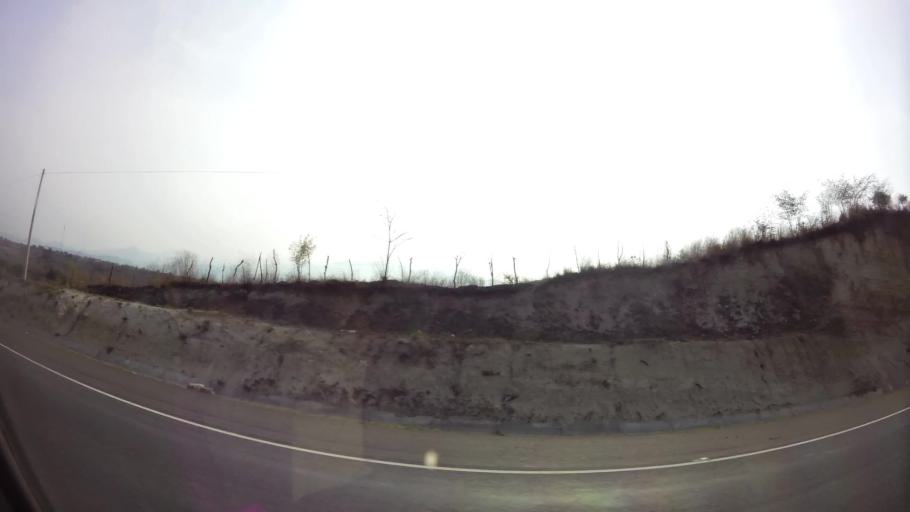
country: HN
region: Comayagua
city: Comayagua
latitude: 14.4108
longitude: -87.6225
